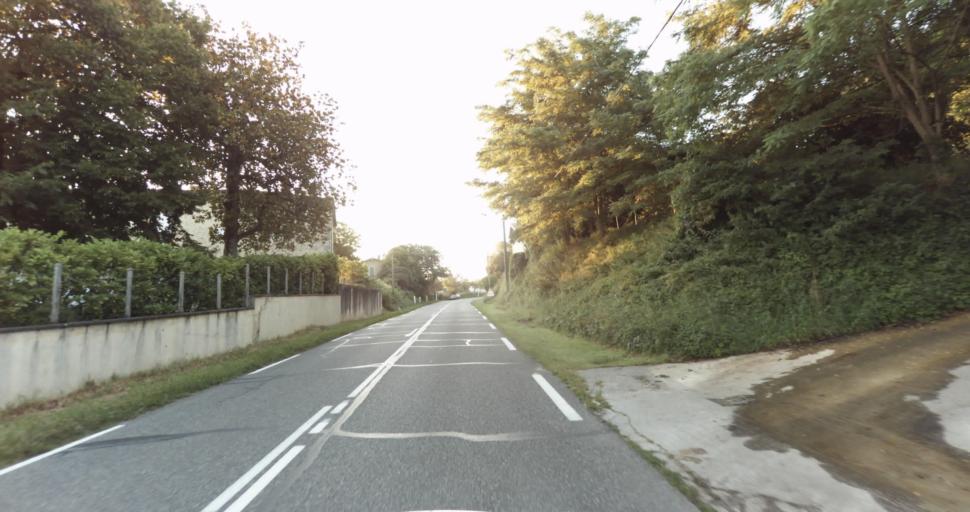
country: FR
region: Aquitaine
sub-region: Departement de la Gironde
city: Bazas
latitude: 44.4311
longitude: -0.1993
